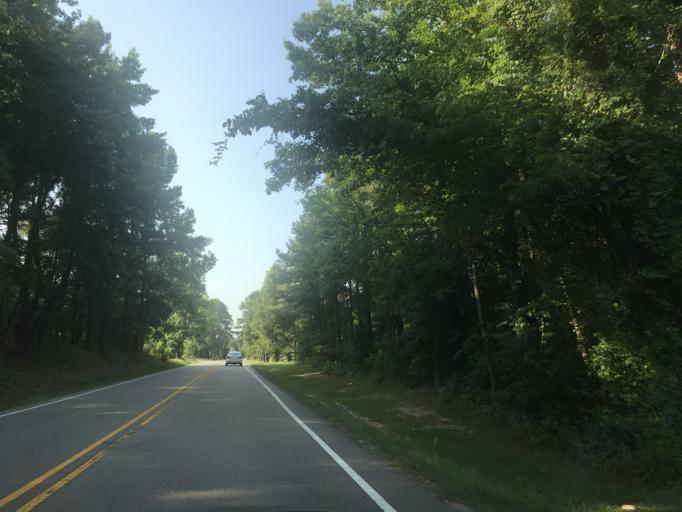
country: US
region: North Carolina
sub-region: Wake County
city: Knightdale
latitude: 35.8473
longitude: -78.5010
